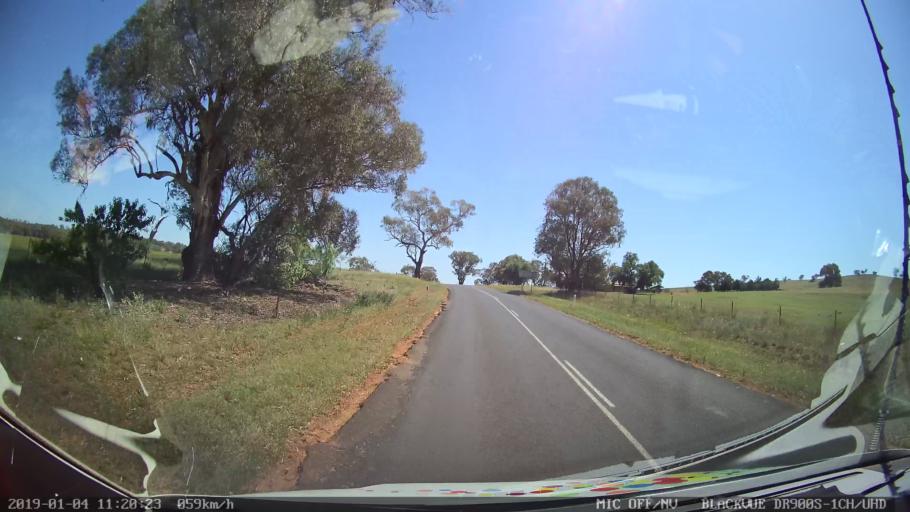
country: AU
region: New South Wales
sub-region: Cabonne
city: Molong
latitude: -33.1643
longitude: 148.7065
